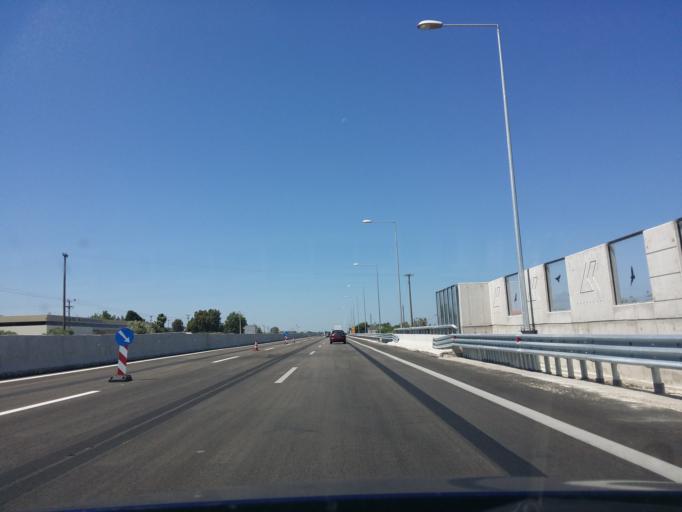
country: GR
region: West Greece
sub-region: Nomos Achaias
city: Rio
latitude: 38.3087
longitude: 21.8116
